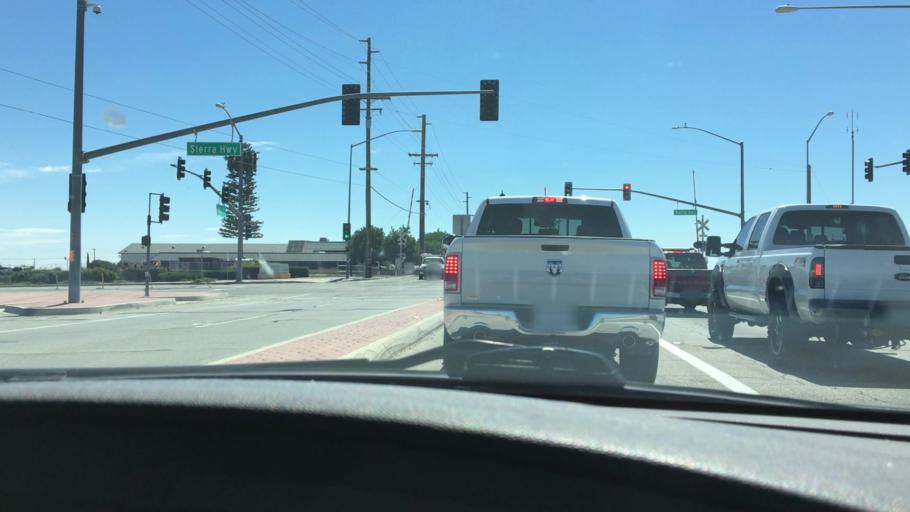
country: US
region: California
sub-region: Los Angeles County
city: Lancaster
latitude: 34.6459
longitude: -118.1289
